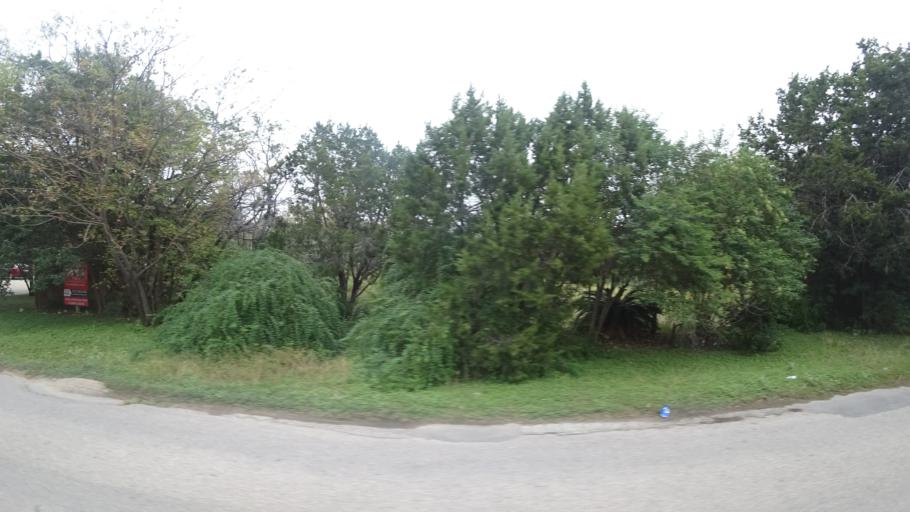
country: US
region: Texas
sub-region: Travis County
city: Hudson Bend
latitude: 30.3737
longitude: -97.9278
